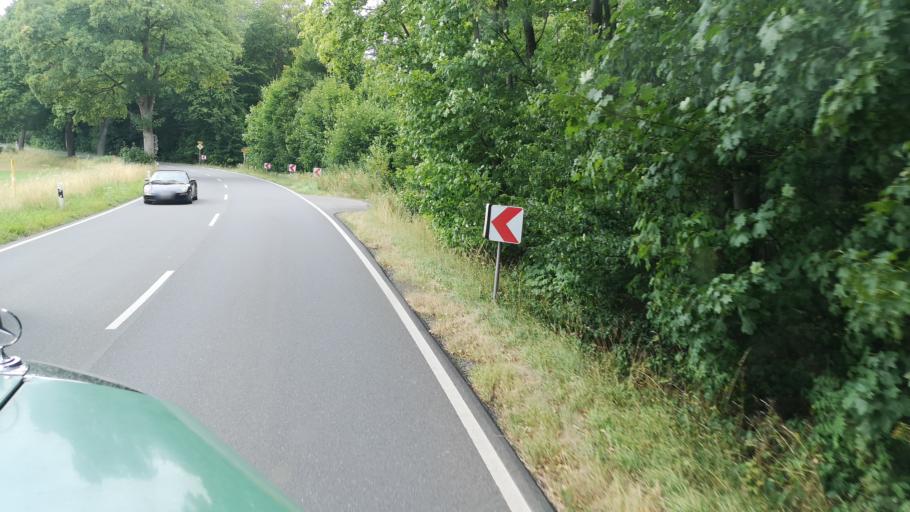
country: DE
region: North Rhine-Westphalia
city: Huckeswagen
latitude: 51.1551
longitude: 7.2861
